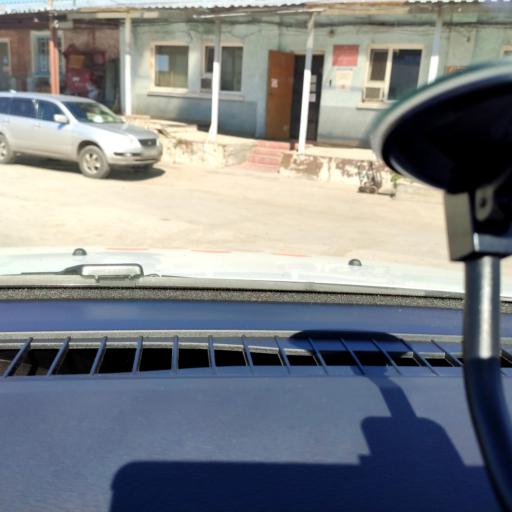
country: RU
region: Samara
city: Smyshlyayevka
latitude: 53.2134
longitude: 50.2751
